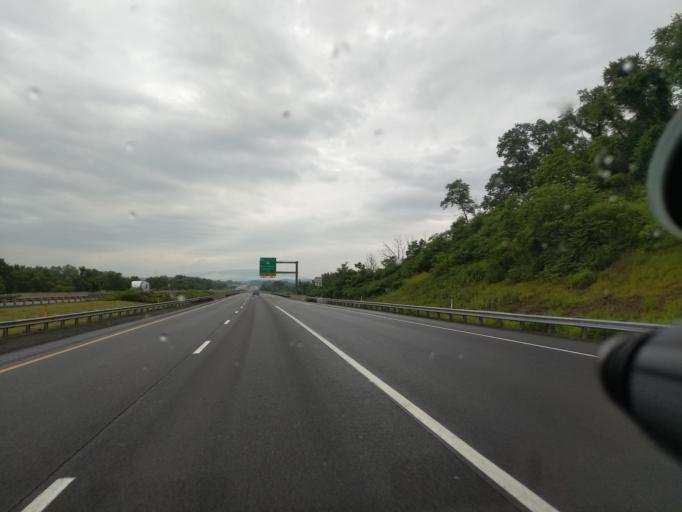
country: US
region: Pennsylvania
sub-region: Union County
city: New Columbia
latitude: 41.0516
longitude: -76.8482
